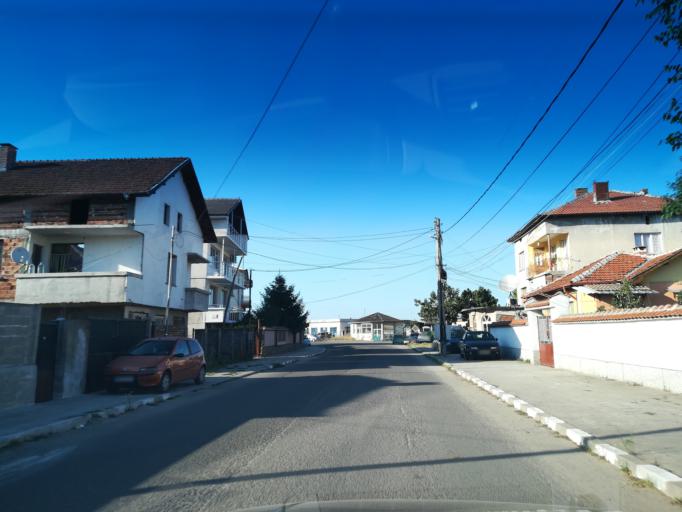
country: BG
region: Stara Zagora
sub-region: Obshtina Chirpan
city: Chirpan
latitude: 42.1063
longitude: 25.2214
